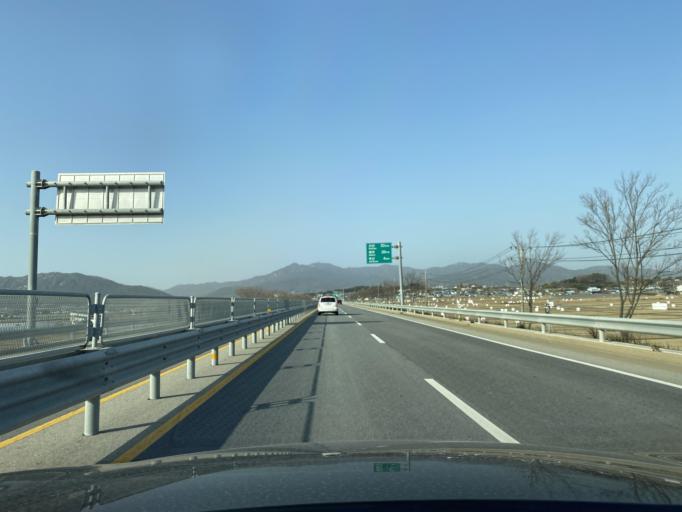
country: KR
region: Chungcheongnam-do
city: Hongsung
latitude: 36.6894
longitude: 126.7089
